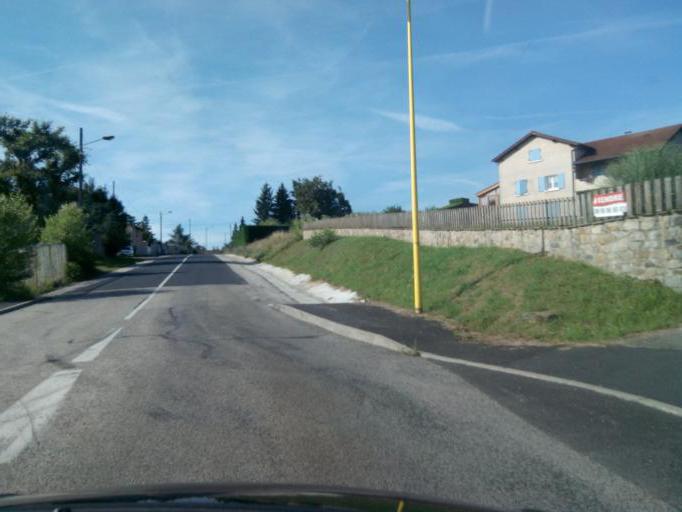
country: FR
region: Auvergne
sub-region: Departement de la Haute-Loire
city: Bas-en-Basset
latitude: 45.2974
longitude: 4.1160
